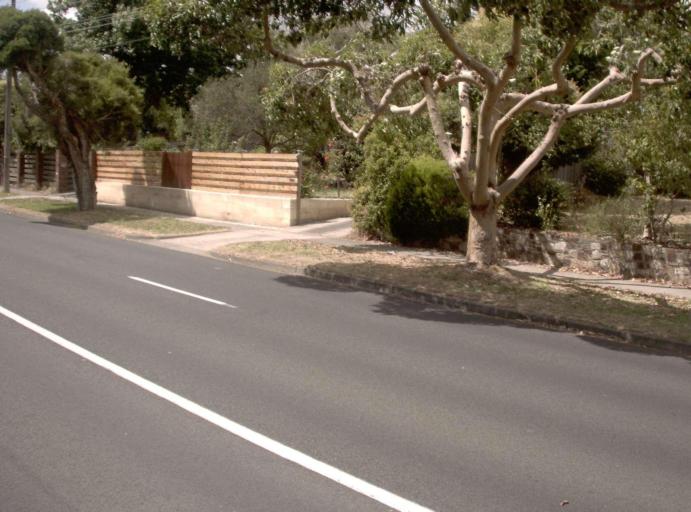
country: AU
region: Victoria
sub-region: Whitehorse
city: Burwood
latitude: -37.8564
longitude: 145.1220
